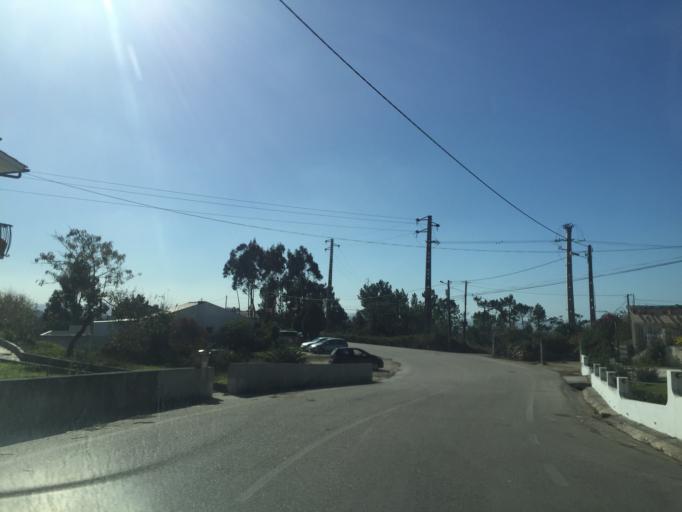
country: PT
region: Coimbra
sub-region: Figueira da Foz
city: Tavarede
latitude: 40.1845
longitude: -8.8379
